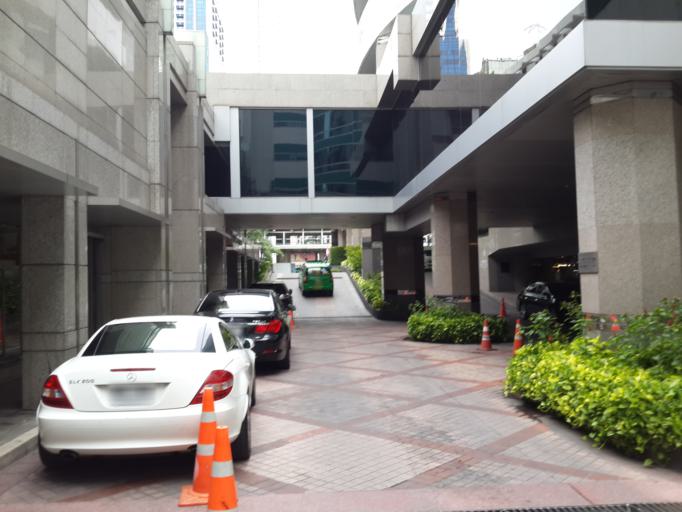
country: TH
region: Bangkok
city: Ratchathewi
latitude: 13.7453
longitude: 100.5416
